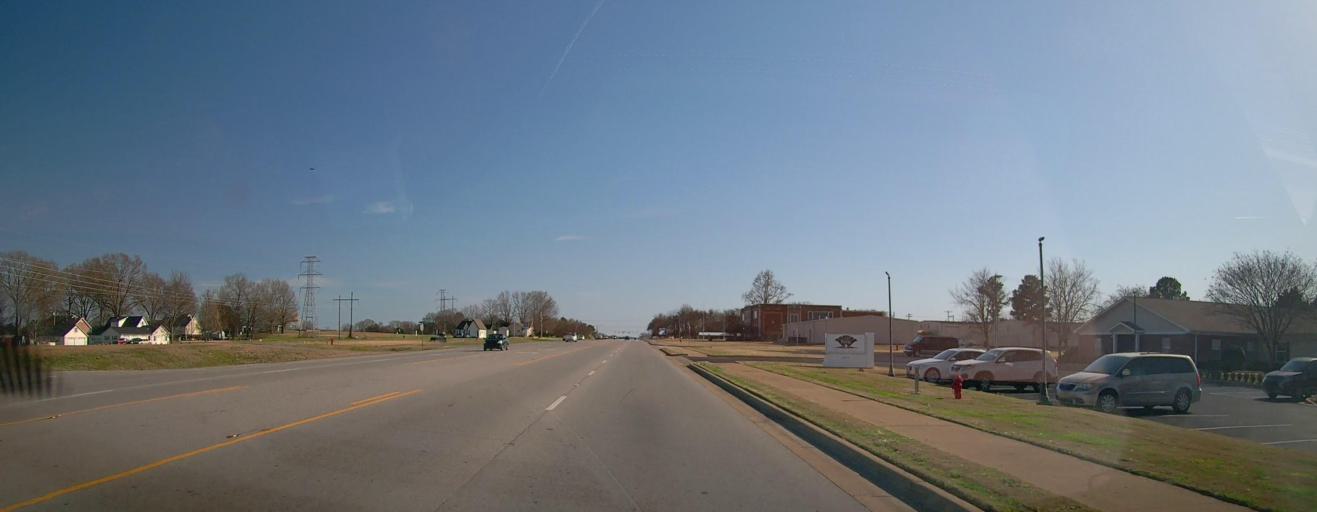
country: US
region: Alabama
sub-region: Colbert County
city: Muscle Shoals
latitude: 34.7356
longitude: -87.6353
